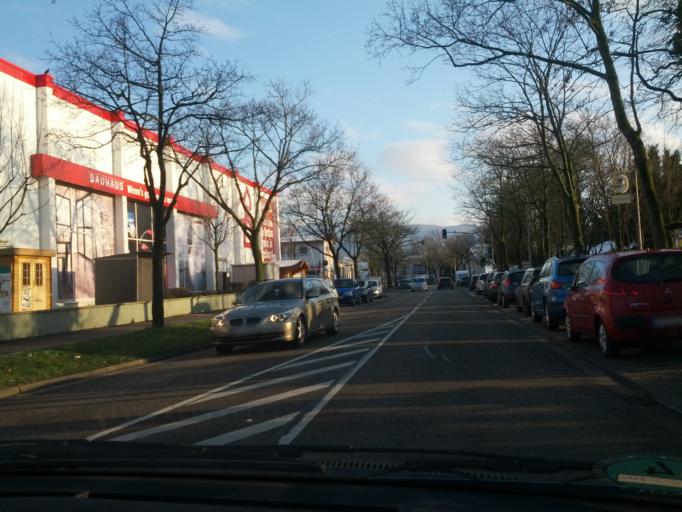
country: DE
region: Baden-Wuerttemberg
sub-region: Freiburg Region
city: Merzhausen
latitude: 47.9832
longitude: 7.8198
